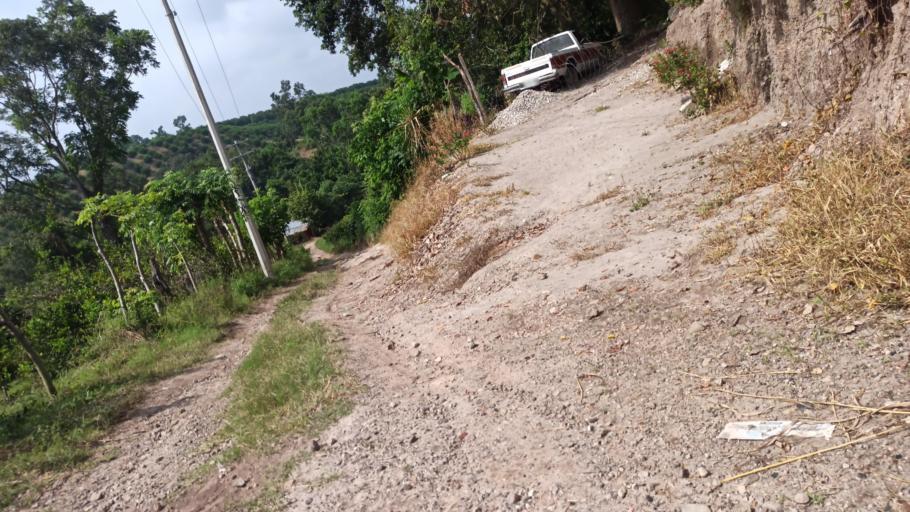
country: MX
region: Puebla
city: San Jose Acateno
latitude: 20.1603
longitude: -97.1816
